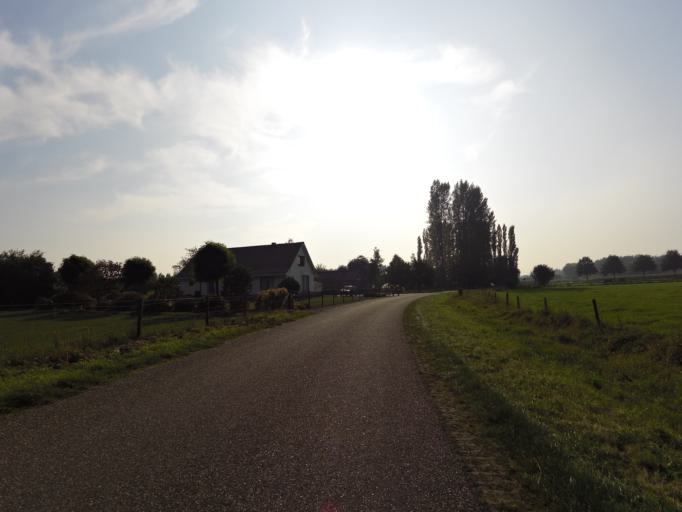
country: NL
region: Gelderland
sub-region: Gemeente Doesburg
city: Doesburg
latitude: 51.9493
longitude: 6.1796
